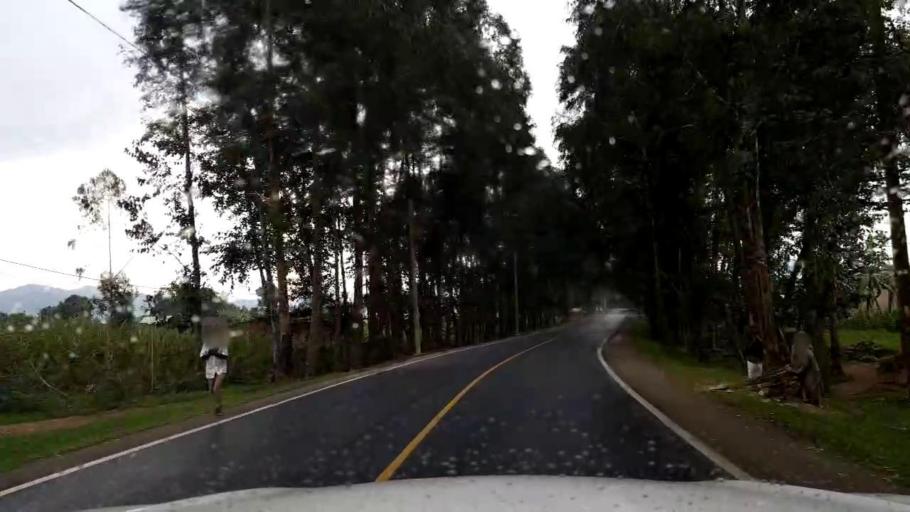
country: RW
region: Western Province
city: Gisenyi
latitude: -1.6723
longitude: 29.3608
